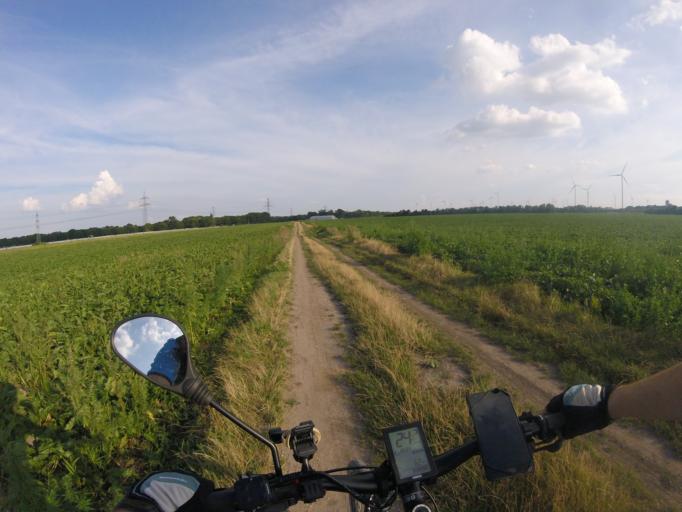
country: AT
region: Lower Austria
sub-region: Politischer Bezirk Baden
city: Ebreichsdorf
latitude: 47.9692
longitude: 16.3707
